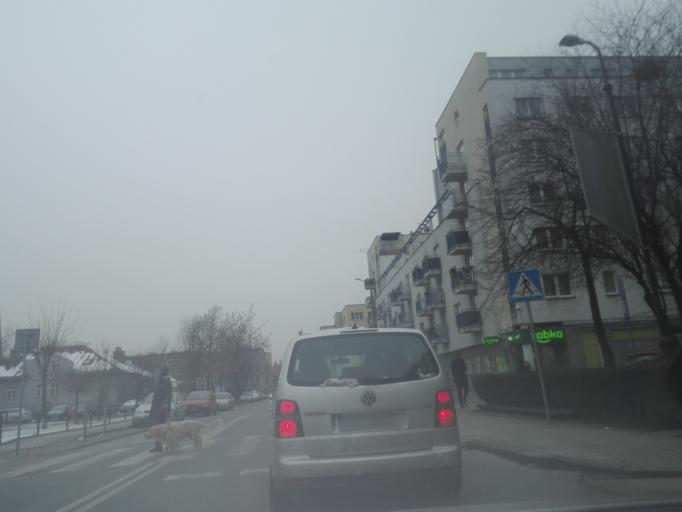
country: PL
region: Silesian Voivodeship
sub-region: Katowice
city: Katowice
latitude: 50.2552
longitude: 19.0377
